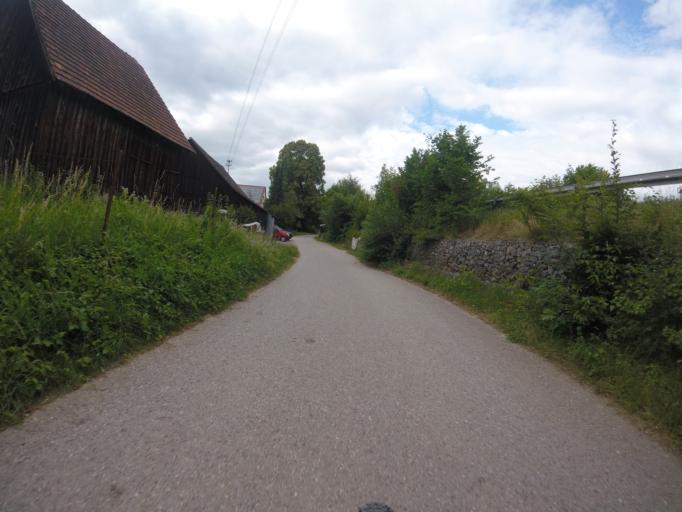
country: DE
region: Baden-Wuerttemberg
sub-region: Regierungsbezirk Stuttgart
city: Oppenweiler
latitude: 48.9708
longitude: 9.4596
